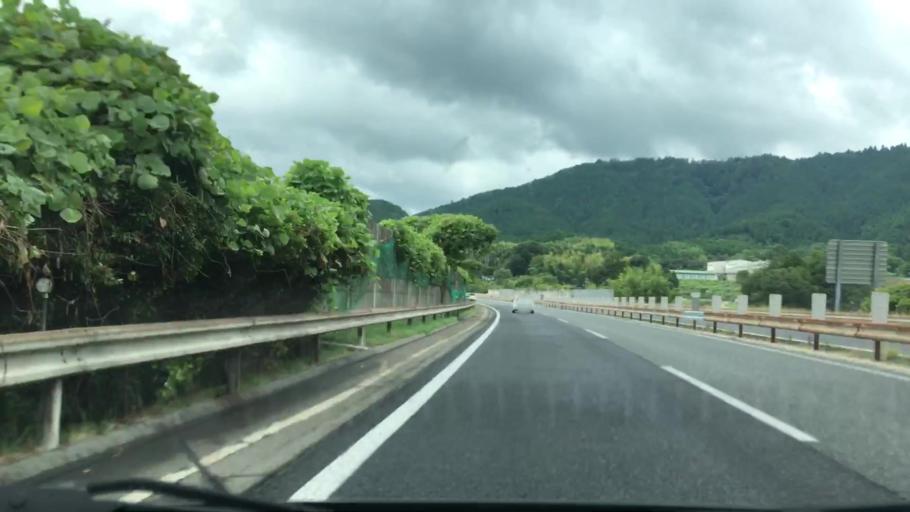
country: JP
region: Okayama
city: Tsuyama
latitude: 35.0223
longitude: 133.7355
